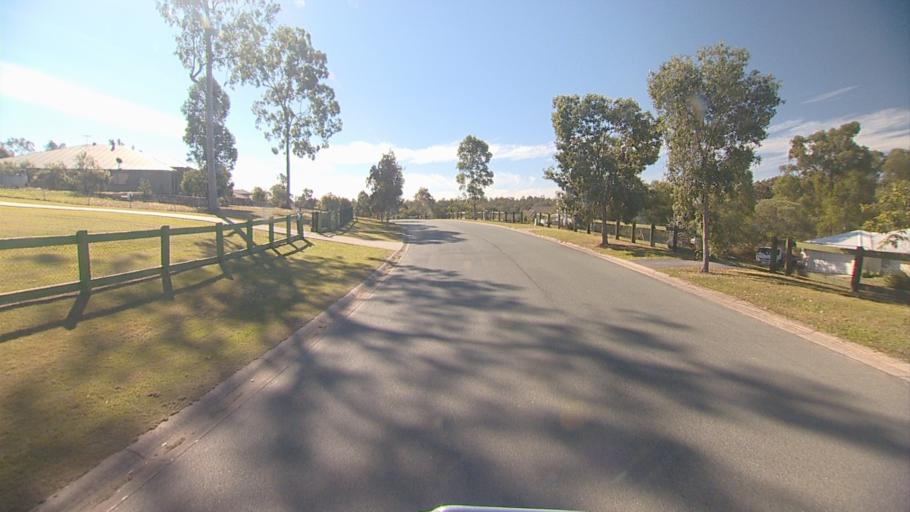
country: AU
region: Queensland
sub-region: Ipswich
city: Springfield Lakes
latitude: -27.7432
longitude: 152.9222
